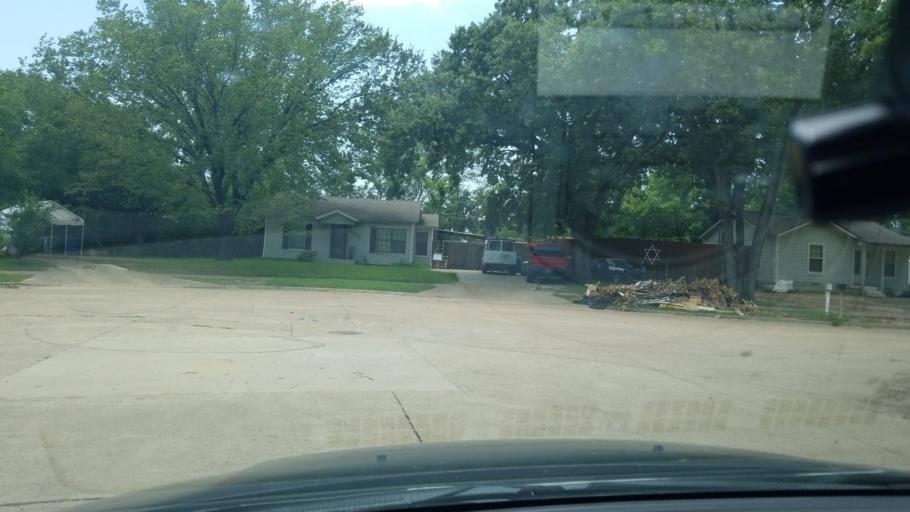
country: US
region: Texas
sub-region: Dallas County
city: Balch Springs
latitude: 32.7164
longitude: -96.6605
